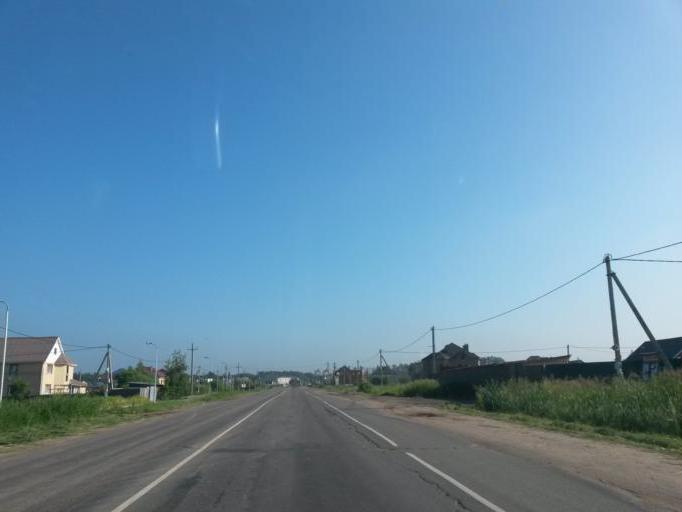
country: RU
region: Moskovskaya
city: Gorki-Leninskiye
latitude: 55.4993
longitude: 37.7803
